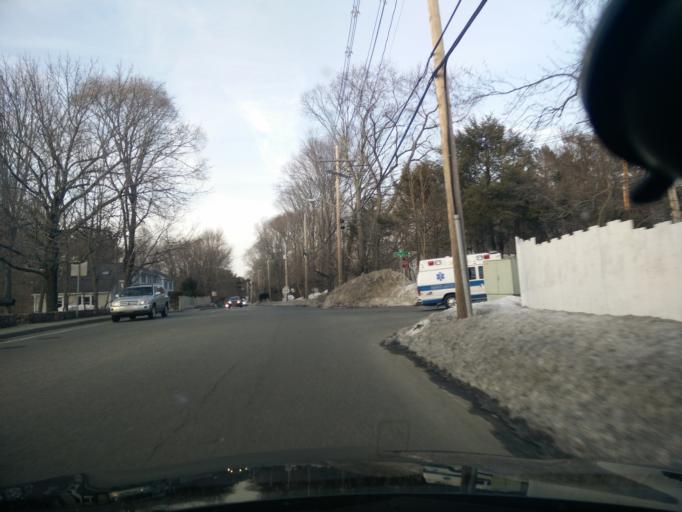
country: US
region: Massachusetts
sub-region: Norfolk County
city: Westwood
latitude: 42.2329
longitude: -71.2193
